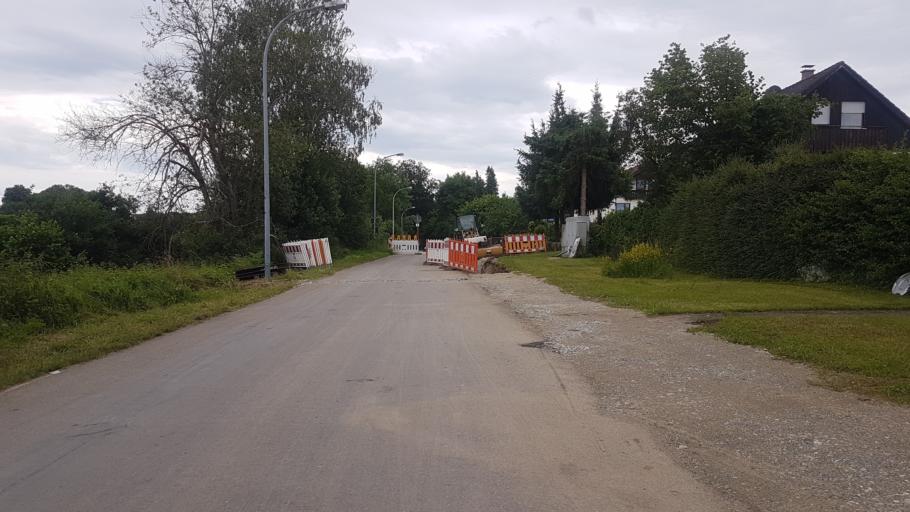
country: DE
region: Baden-Wuerttemberg
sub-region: Tuebingen Region
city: Sigmaringendorf
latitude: 48.0695
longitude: 9.2538
